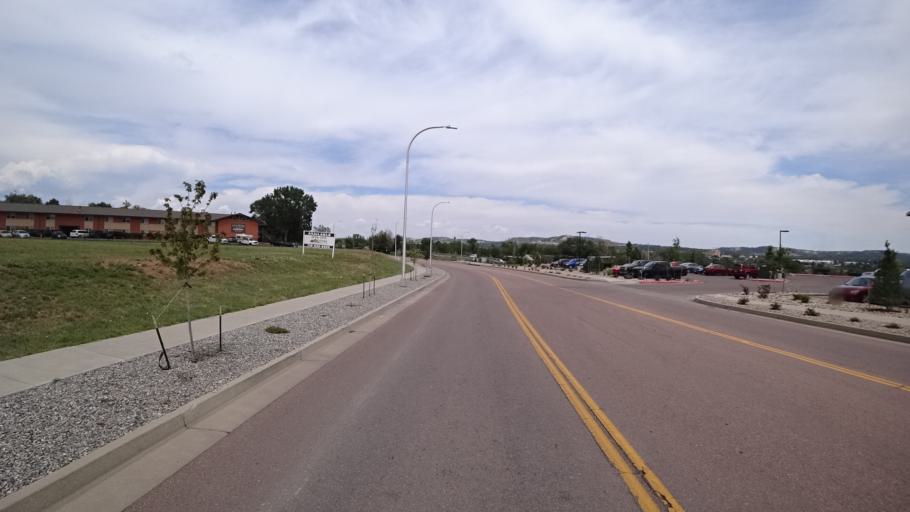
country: US
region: Colorado
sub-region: El Paso County
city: Colorado Springs
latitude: 38.8779
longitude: -104.8368
